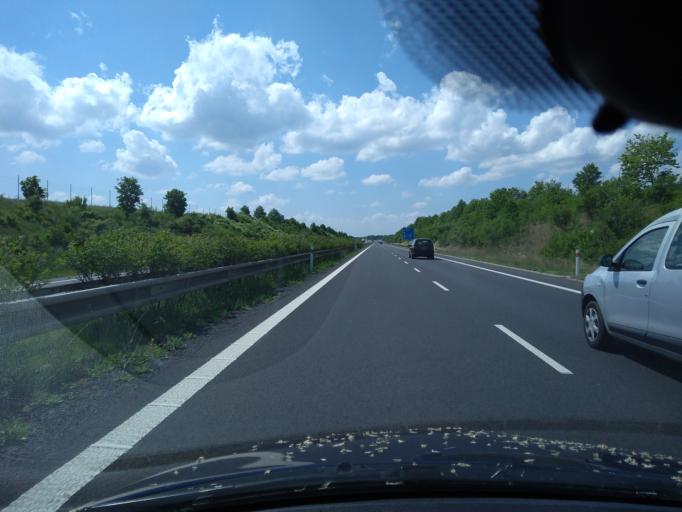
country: CZ
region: Plzensky
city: Stenovice
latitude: 49.6689
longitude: 13.3518
